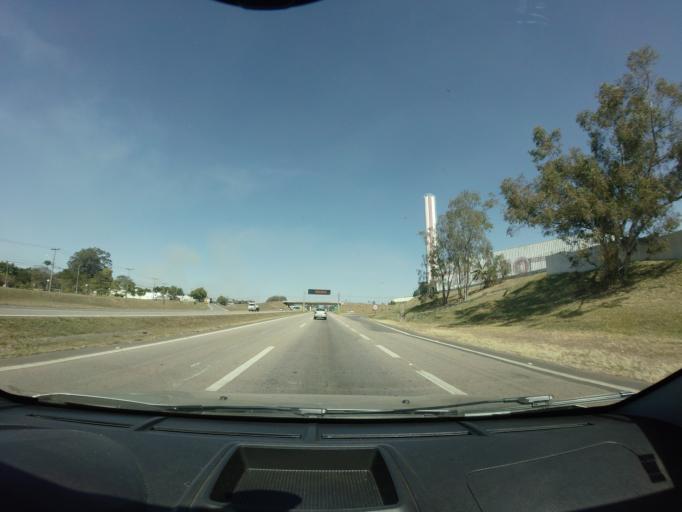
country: BR
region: Sao Paulo
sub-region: Piracicaba
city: Piracicaba
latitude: -22.7402
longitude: -47.6010
